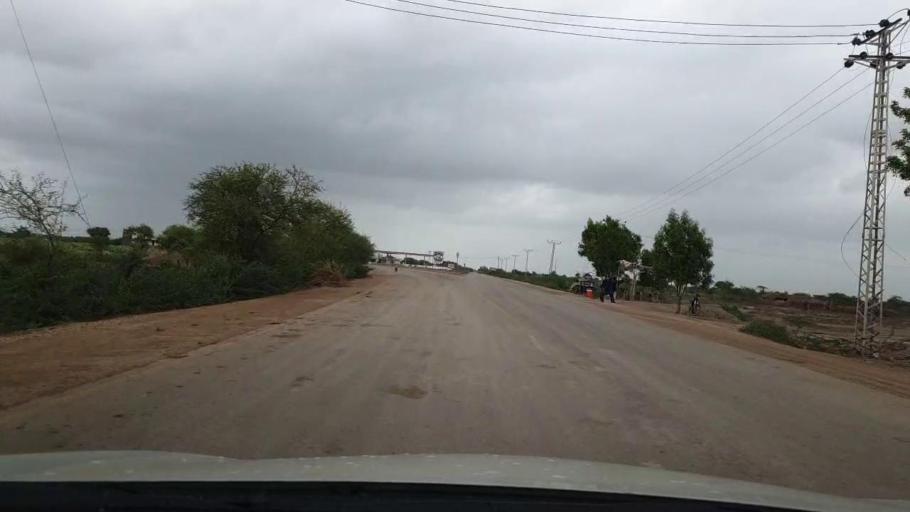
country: PK
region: Sindh
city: Badin
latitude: 24.6523
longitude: 68.7735
